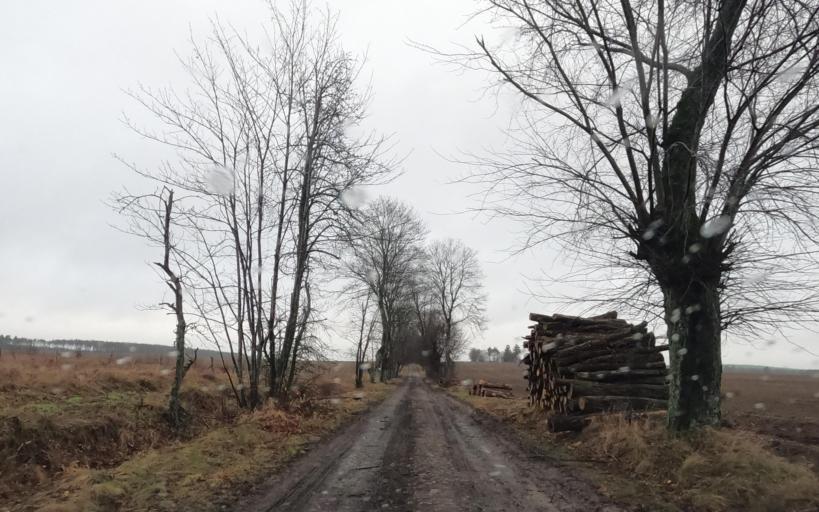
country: PL
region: West Pomeranian Voivodeship
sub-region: Powiat szczecinecki
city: Szczecinek
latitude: 53.6153
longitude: 16.6704
